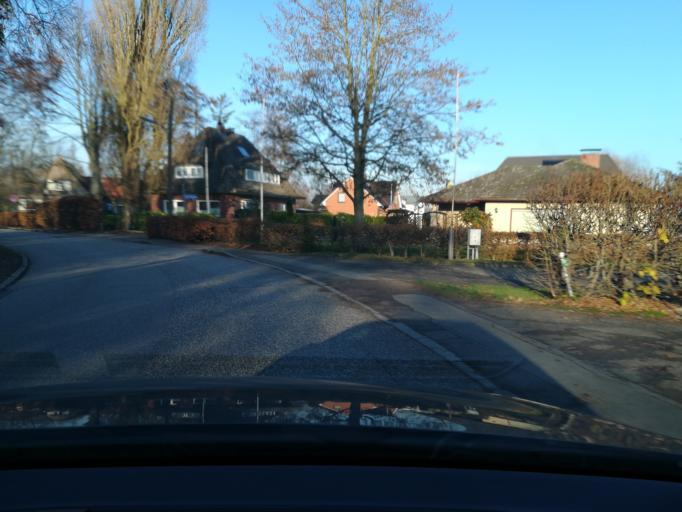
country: DE
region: Lower Saxony
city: Stelle
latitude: 53.4464
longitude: 10.1340
